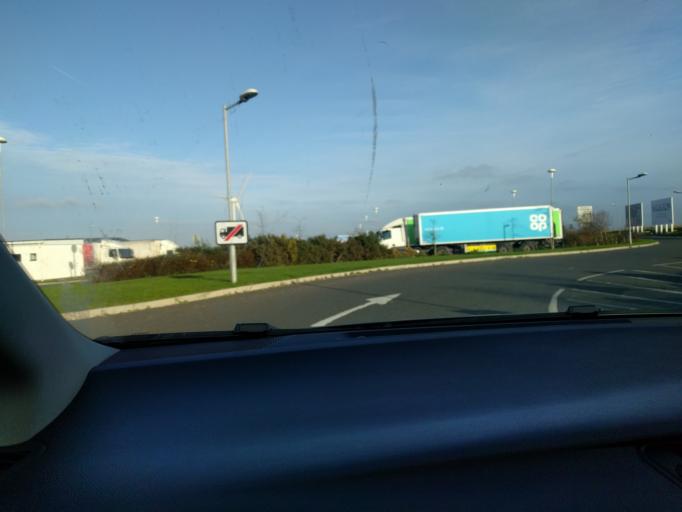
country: GB
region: England
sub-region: Cornwall
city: Roche
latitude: 50.4247
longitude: -4.8178
